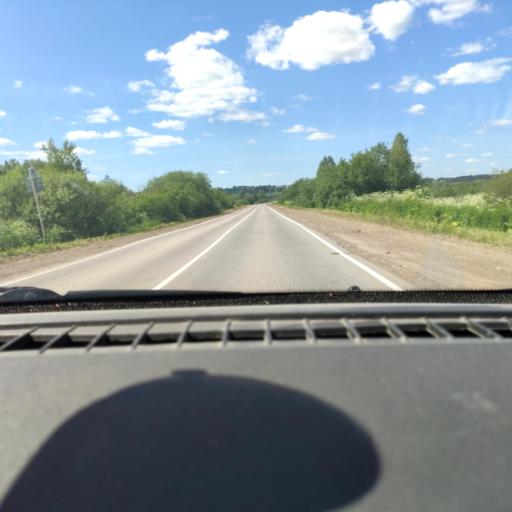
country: RU
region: Perm
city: Chaykovskaya
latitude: 58.0923
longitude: 55.6056
